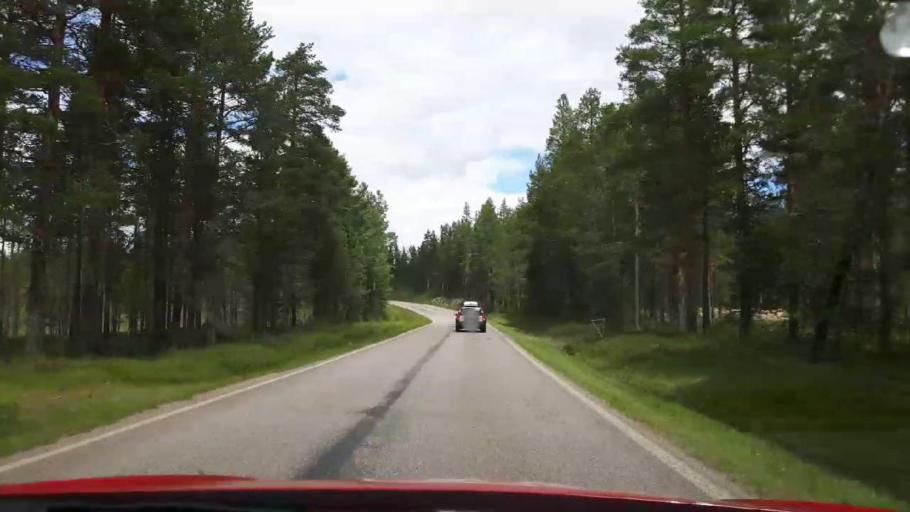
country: NO
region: Hedmark
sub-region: Trysil
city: Innbygda
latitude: 61.8355
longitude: 12.9568
